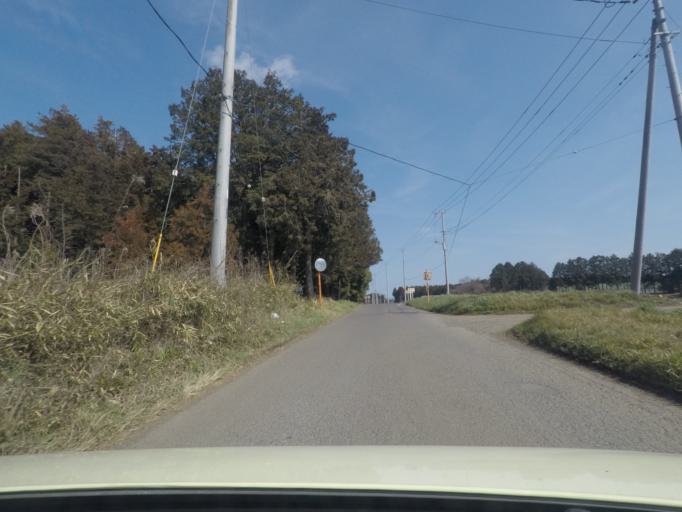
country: JP
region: Ibaraki
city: Okunoya
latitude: 36.1825
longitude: 140.3832
